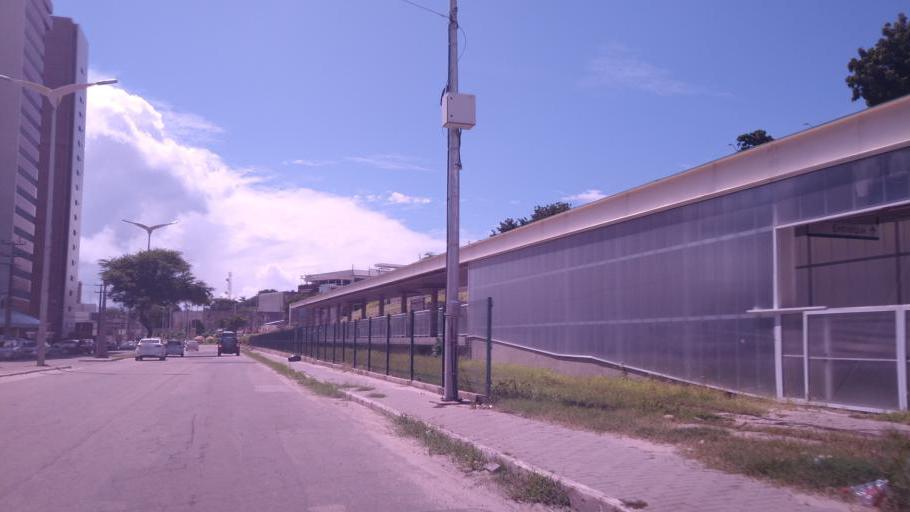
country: BR
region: Ceara
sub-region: Fortaleza
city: Fortaleza
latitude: -3.7208
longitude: -38.4774
